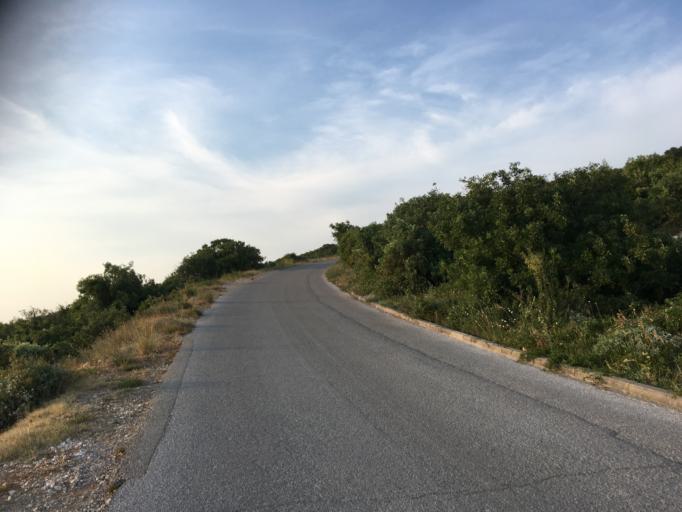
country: HR
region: Primorsko-Goranska
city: Punat
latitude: 44.9925
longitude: 14.6313
